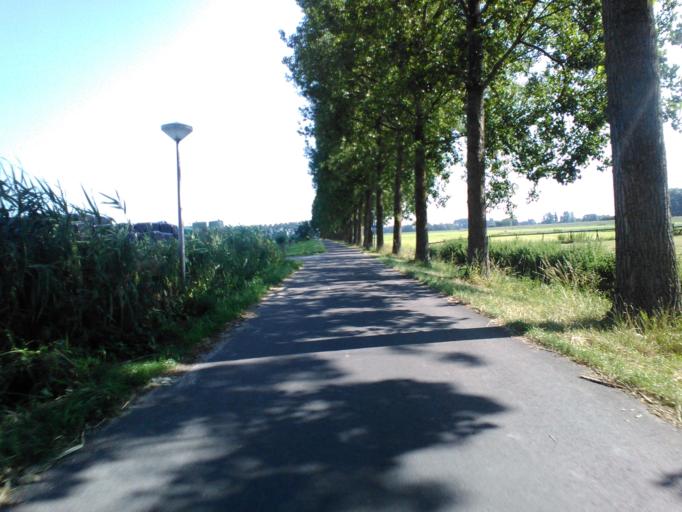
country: NL
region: South Holland
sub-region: Gemeente Alphen aan den Rijn
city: Alphen aan den Rijn
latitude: 52.1532
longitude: 4.6929
